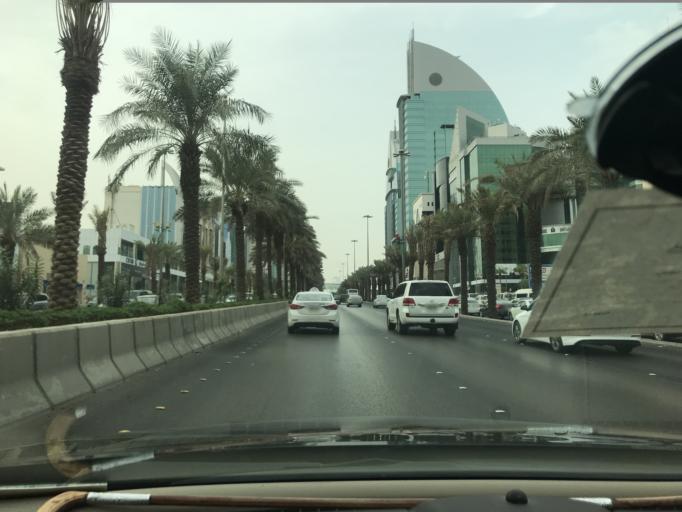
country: SA
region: Ar Riyad
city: Riyadh
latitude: 24.7036
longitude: 46.6764
